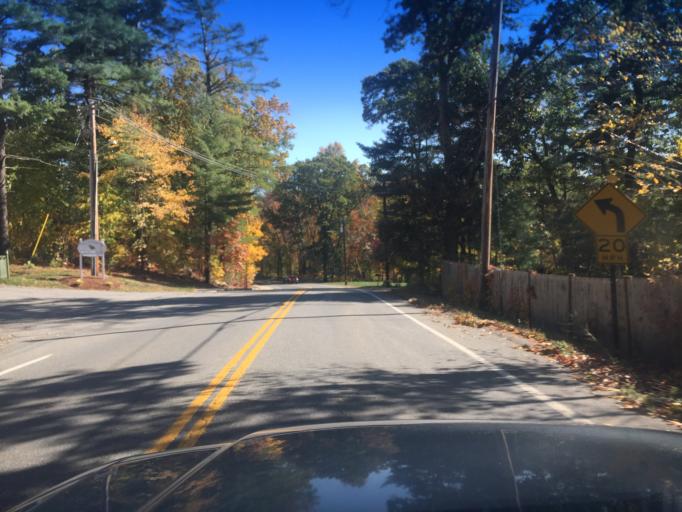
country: US
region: Massachusetts
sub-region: Middlesex County
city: Hudson
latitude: 42.3771
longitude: -71.5559
